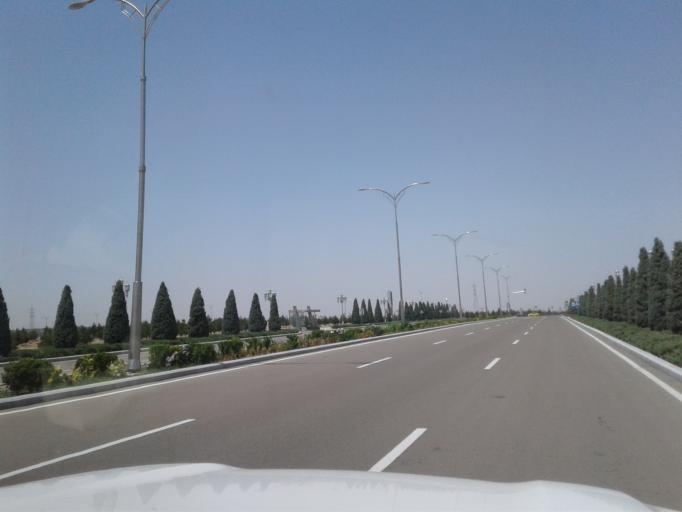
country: TM
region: Balkan
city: Turkmenbasy
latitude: 39.9630
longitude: 52.8647
